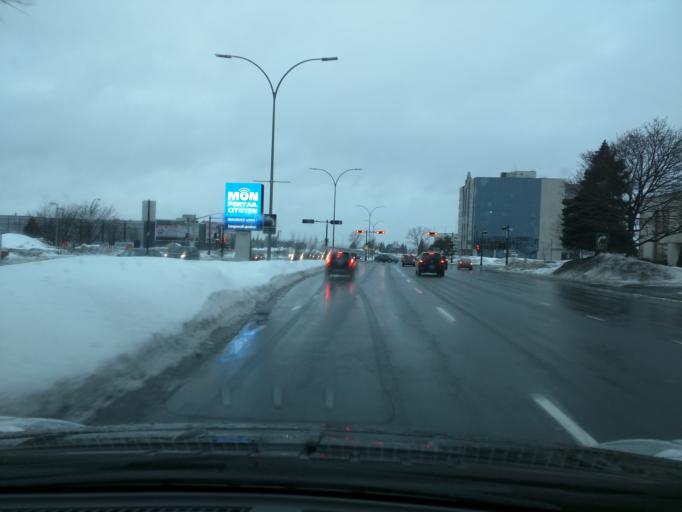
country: CA
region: Quebec
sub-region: Monteregie
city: Longueuil
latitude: 45.5475
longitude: -73.4946
